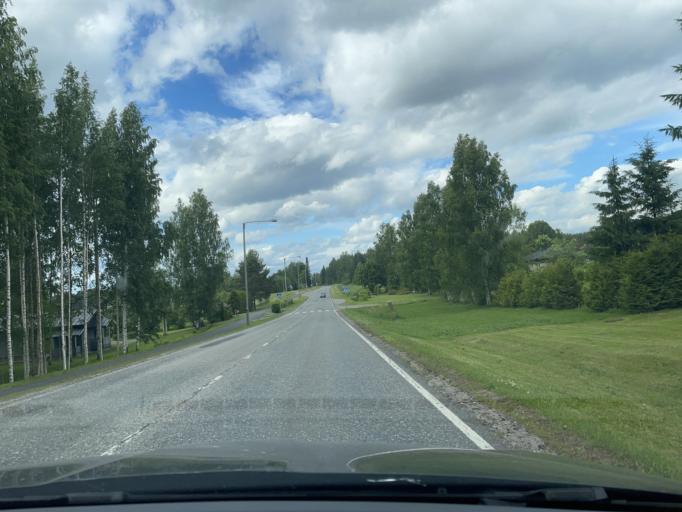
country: FI
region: Central Finland
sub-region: Jaemsae
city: Jaemsaenkoski
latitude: 61.9495
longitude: 25.1516
